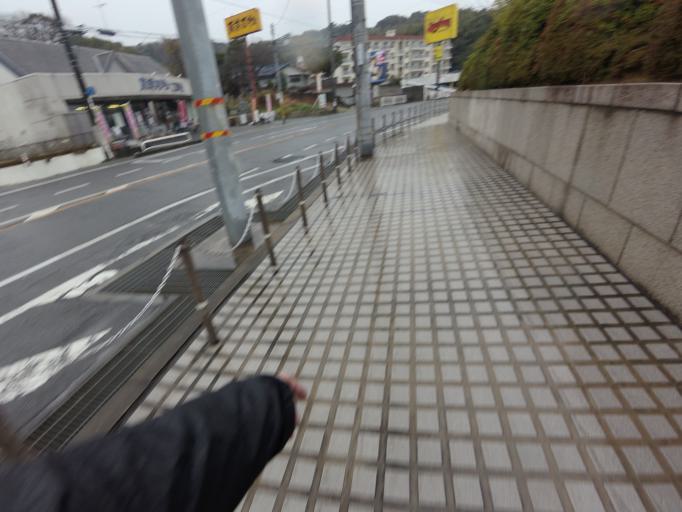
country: JP
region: Okayama
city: Kurashiki
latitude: 34.5954
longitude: 133.7773
